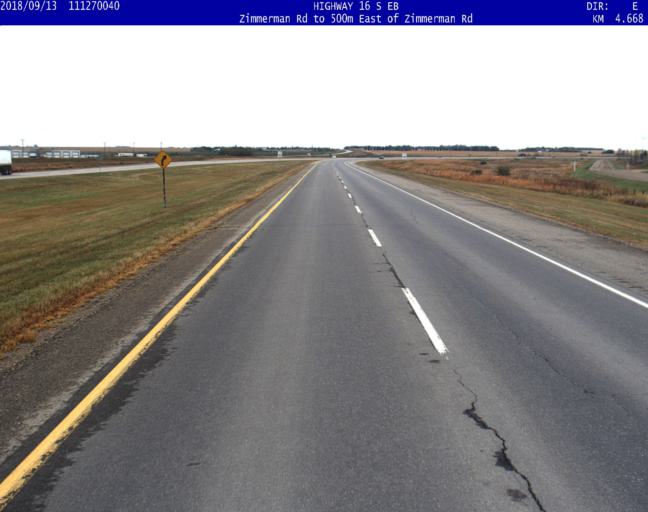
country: CA
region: Saskatchewan
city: Saskatoon
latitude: 52.0859
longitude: -106.5305
